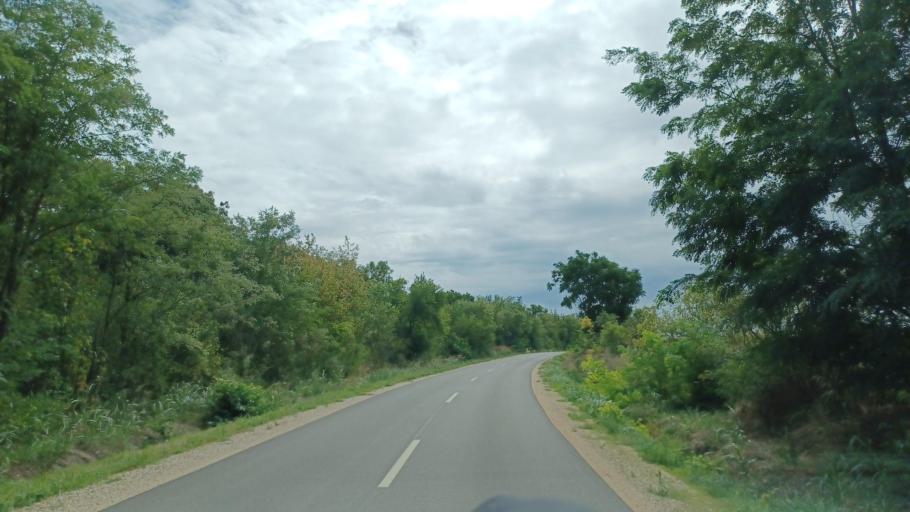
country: HU
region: Tolna
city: Zomba
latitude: 46.4424
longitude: 18.6072
